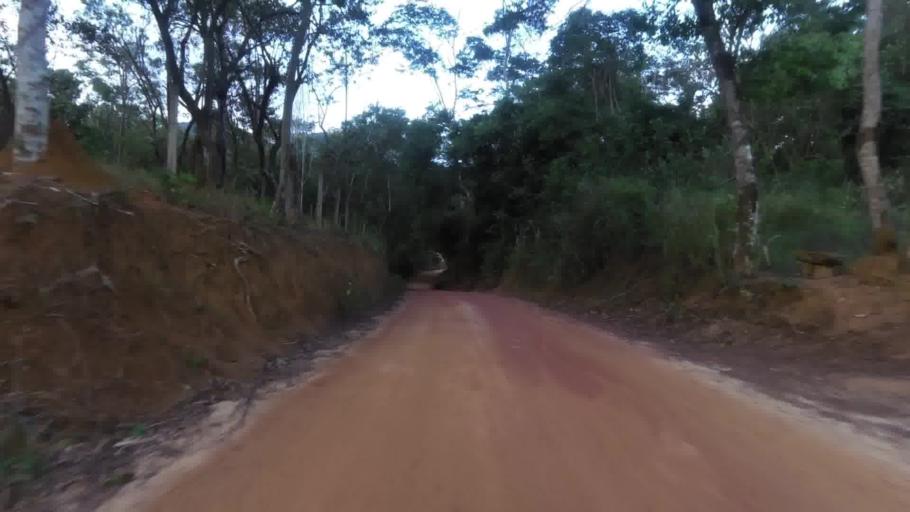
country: BR
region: Espirito Santo
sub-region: Guarapari
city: Guarapari
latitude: -20.6718
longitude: -40.6138
